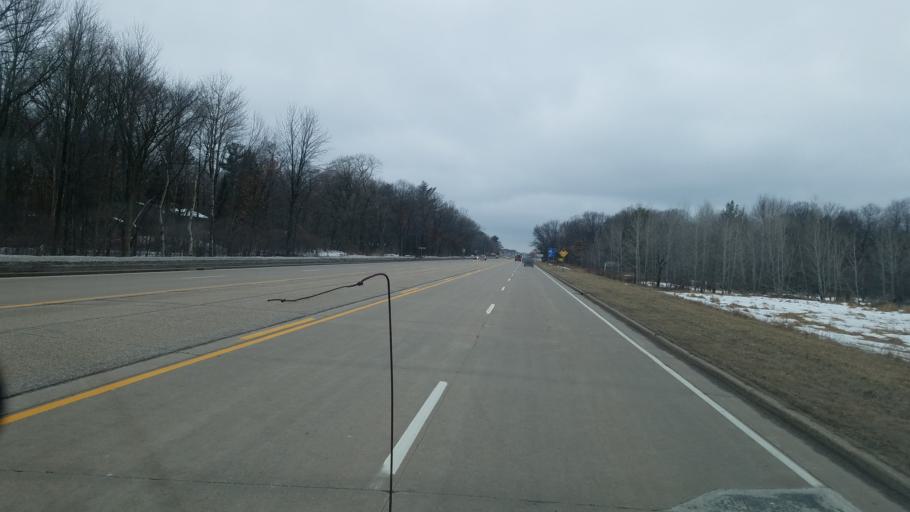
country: US
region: Wisconsin
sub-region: Portage County
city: Whiting
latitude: 44.5240
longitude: -89.4932
